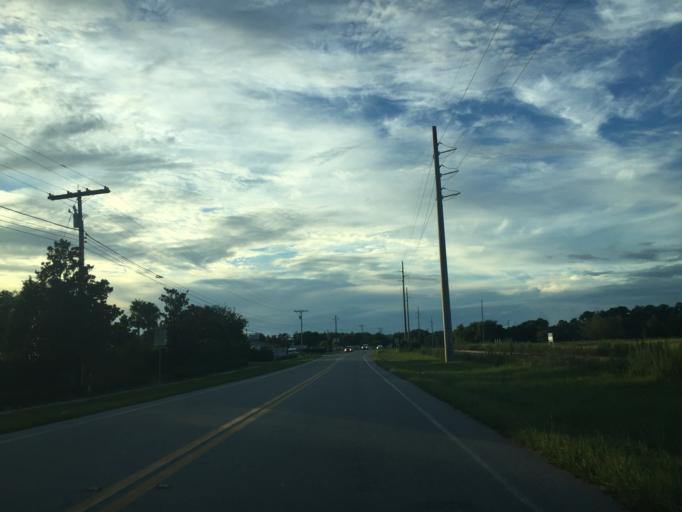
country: US
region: Florida
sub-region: Lake County
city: Tavares
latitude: 28.7779
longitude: -81.7448
